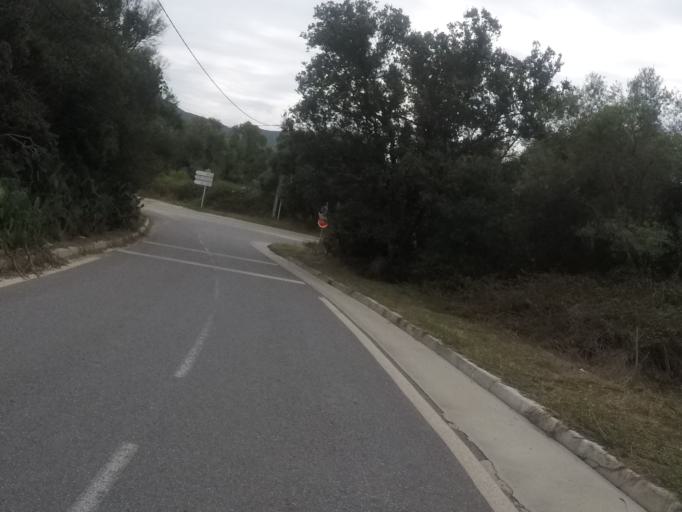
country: FR
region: Corsica
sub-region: Departement de la Corse-du-Sud
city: Propriano
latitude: 41.7290
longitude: 8.8292
